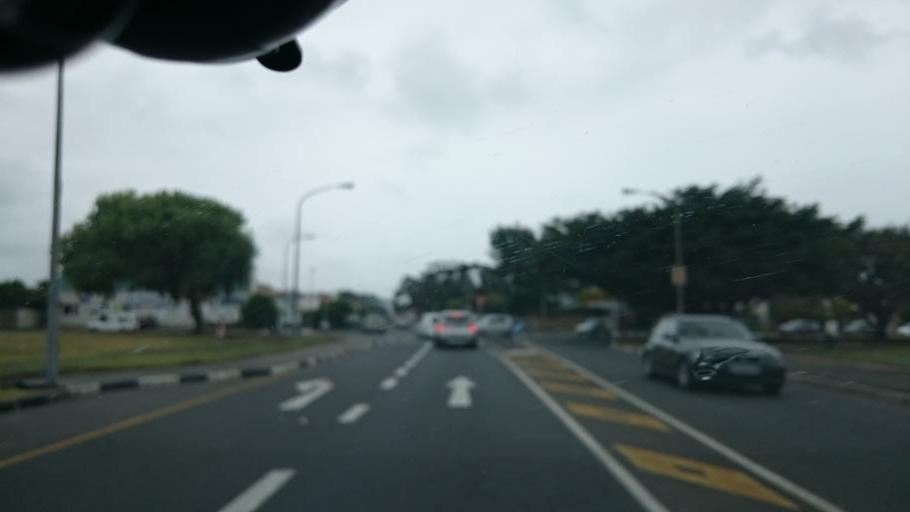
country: ZA
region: Western Cape
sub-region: City of Cape Town
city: Bergvliet
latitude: -34.0341
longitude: 18.4599
